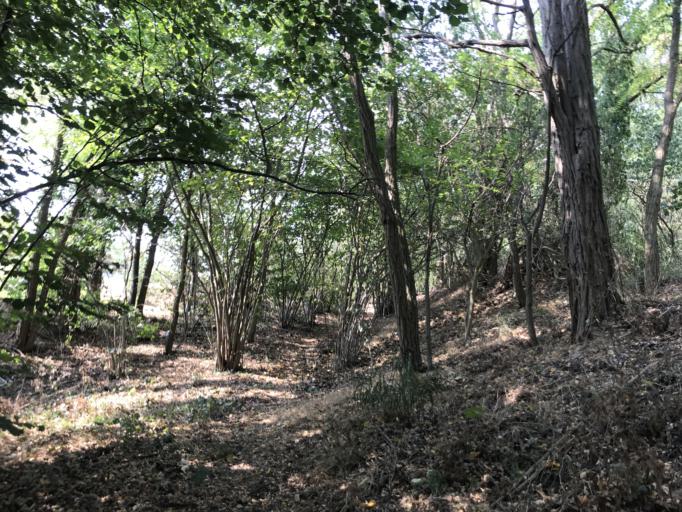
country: DE
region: Rheinland-Pfalz
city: Budenheim
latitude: 50.0030
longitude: 8.1853
